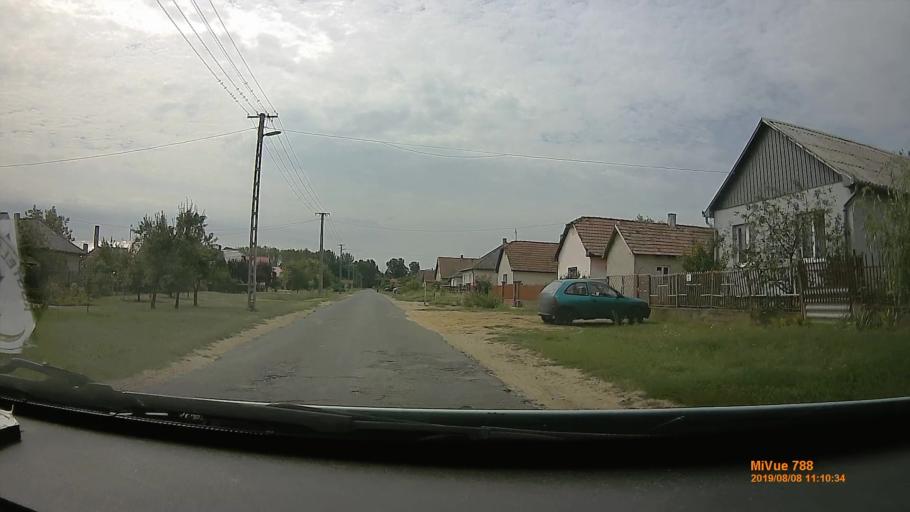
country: HU
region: Szabolcs-Szatmar-Bereg
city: Balkany
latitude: 47.7458
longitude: 21.8397
